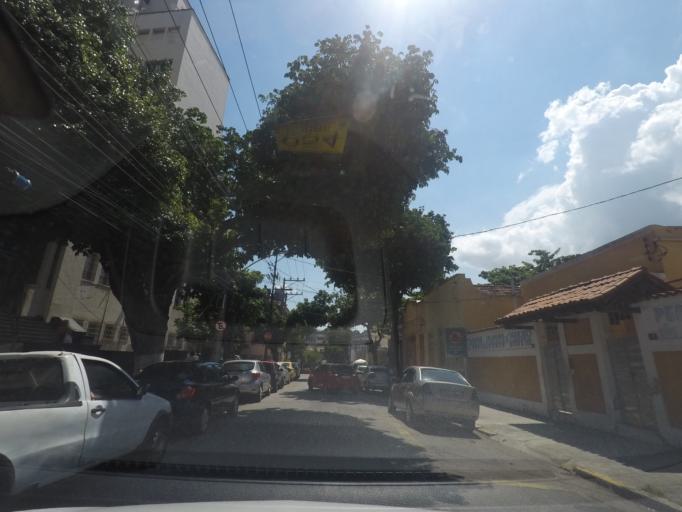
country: BR
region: Rio de Janeiro
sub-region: Rio De Janeiro
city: Rio de Janeiro
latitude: -22.8948
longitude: -43.2255
